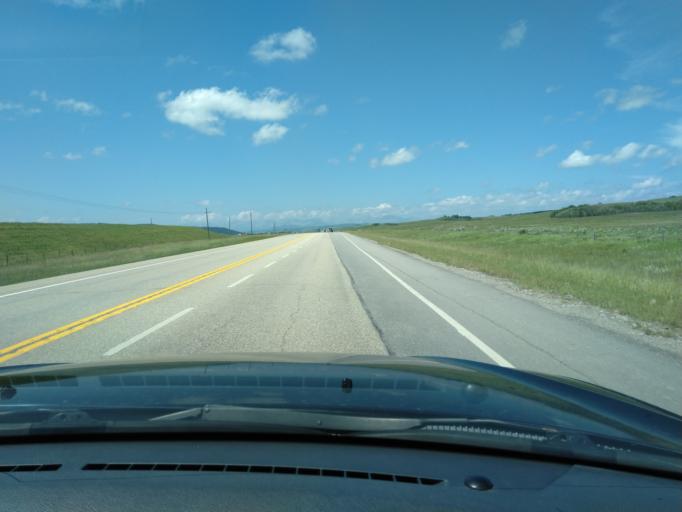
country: CA
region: Alberta
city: Cochrane
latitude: 51.2261
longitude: -114.5947
